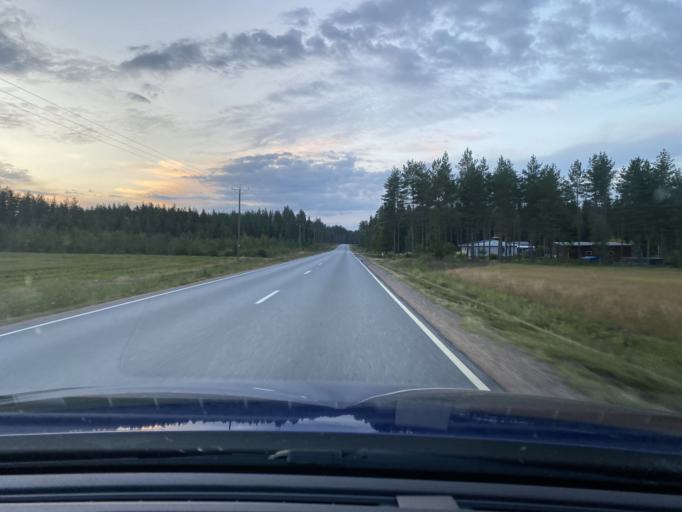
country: FI
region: Satakunta
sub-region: Pohjois-Satakunta
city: Honkajoki
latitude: 62.1085
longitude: 22.2436
